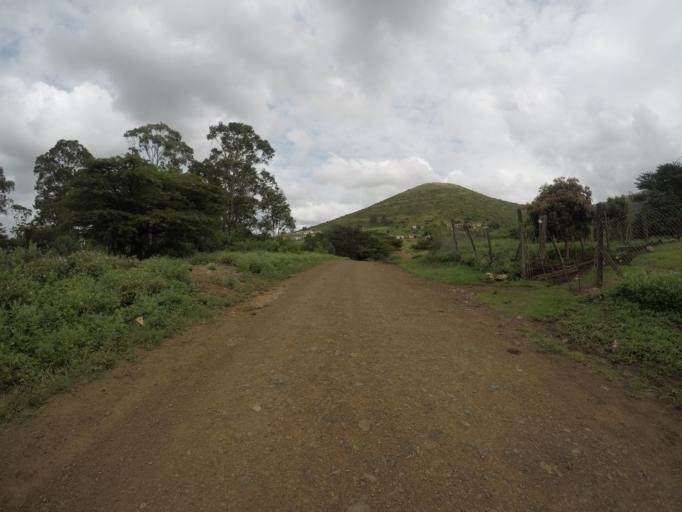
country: ZA
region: KwaZulu-Natal
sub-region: uThungulu District Municipality
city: Empangeni
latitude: -28.5921
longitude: 31.8852
